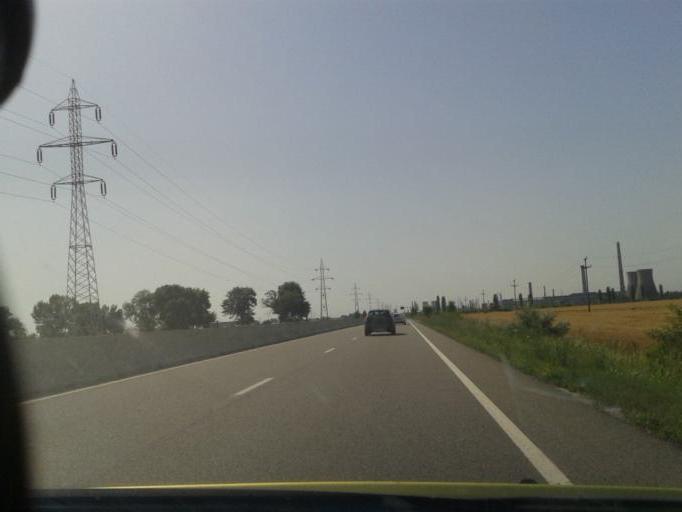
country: RO
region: Prahova
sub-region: Comuna Brazi
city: Negoiesti
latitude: 44.9012
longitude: 26.0004
